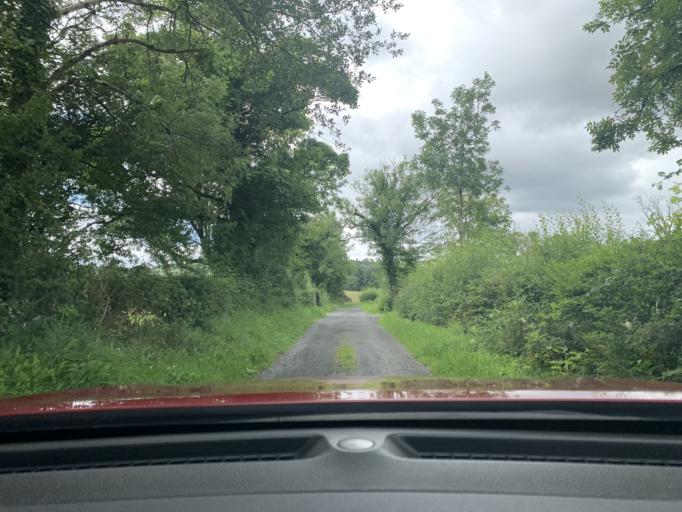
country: GB
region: Northern Ireland
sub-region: Fermanagh District
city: Enniskillen
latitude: 54.2759
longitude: -7.8066
